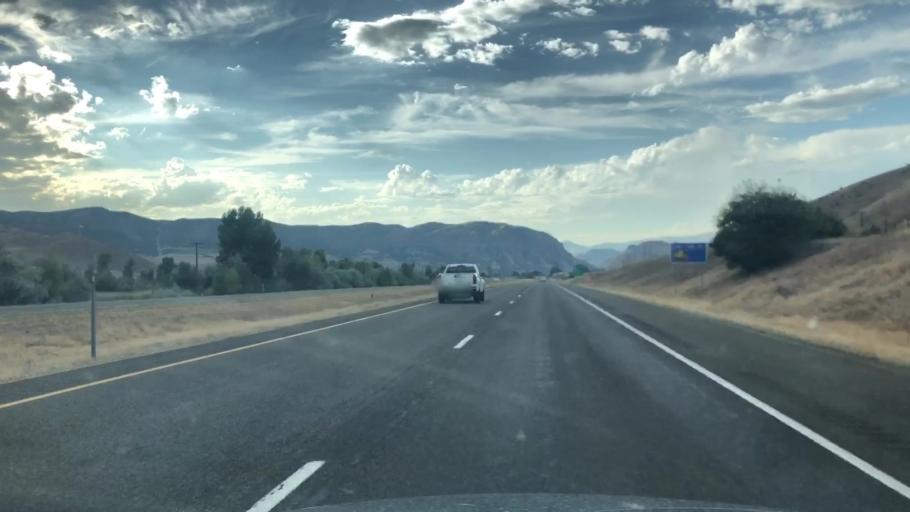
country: US
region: Utah
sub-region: Summit County
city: Coalville
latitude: 41.0032
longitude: -111.4711
